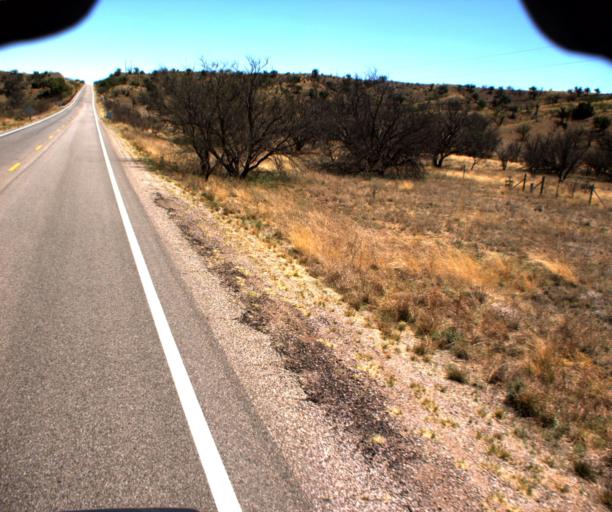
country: US
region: Arizona
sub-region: Pima County
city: Corona de Tucson
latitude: 31.7810
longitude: -110.6925
